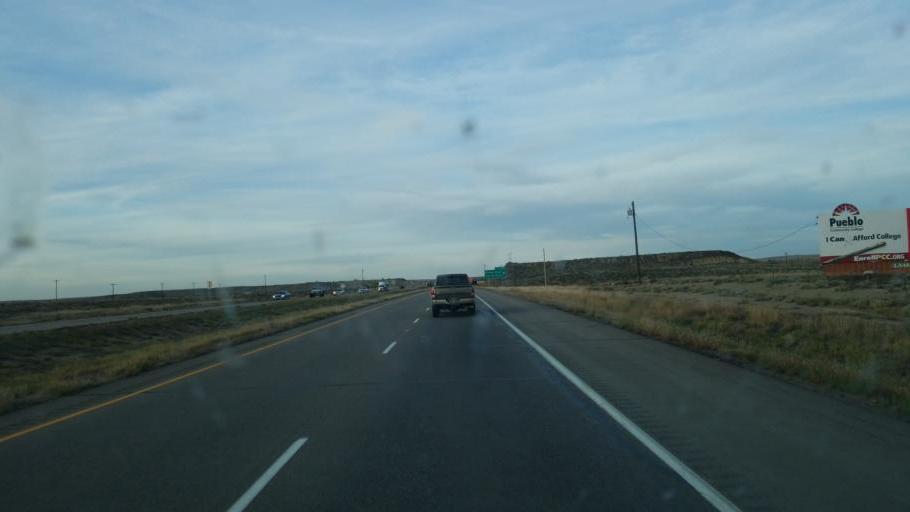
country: US
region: Colorado
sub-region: Pueblo County
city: Pueblo West
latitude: 38.3958
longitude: -104.6190
